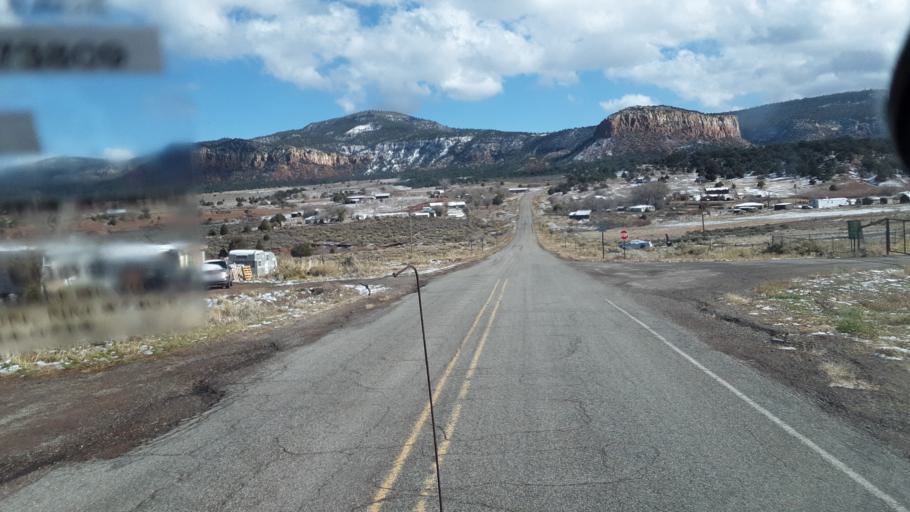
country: US
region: New Mexico
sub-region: Rio Arriba County
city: Santa Teresa
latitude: 36.2295
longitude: -106.8142
